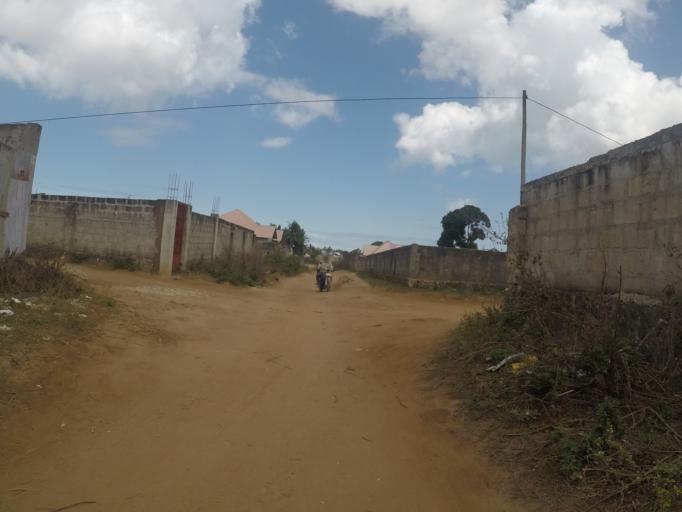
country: TZ
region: Zanzibar Urban/West
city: Zanzibar
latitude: -6.2037
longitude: 39.2318
